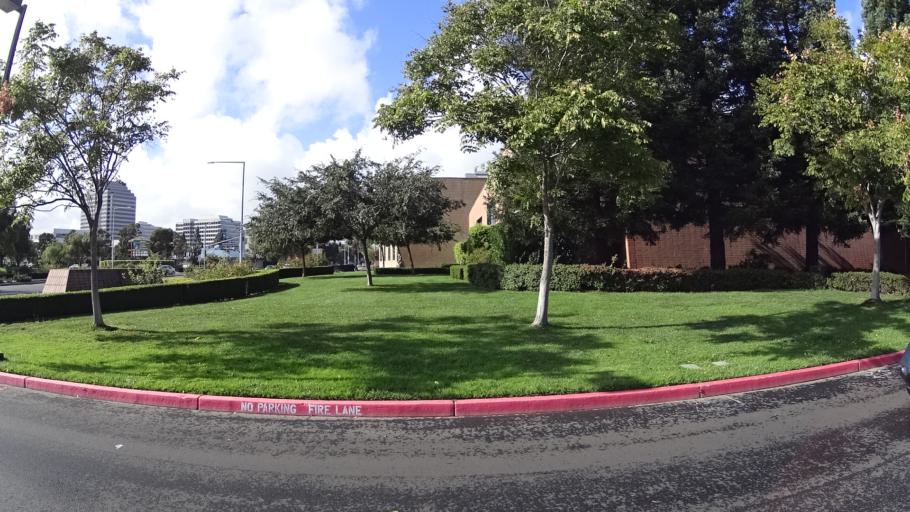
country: US
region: California
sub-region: San Mateo County
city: Foster City
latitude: 37.5582
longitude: -122.2701
